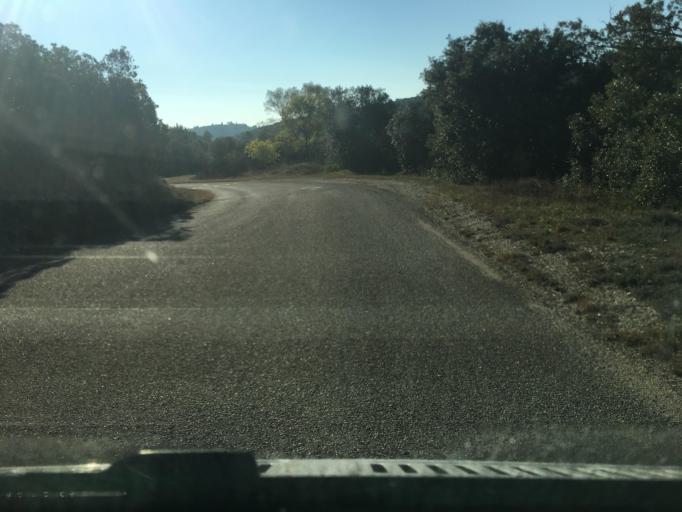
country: FR
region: Languedoc-Roussillon
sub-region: Departement du Gard
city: Goudargues
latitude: 44.1658
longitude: 4.3507
